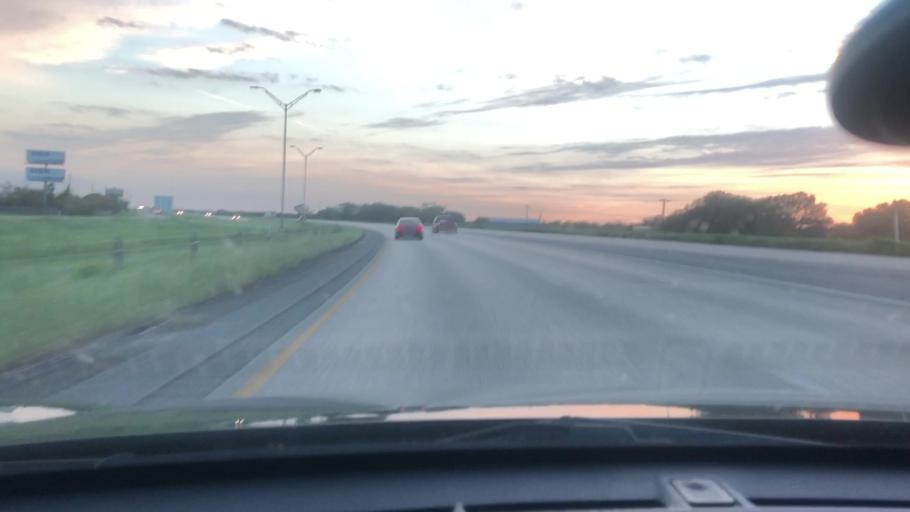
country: US
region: Texas
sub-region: Jackson County
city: Edna
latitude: 28.9817
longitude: -96.6614
